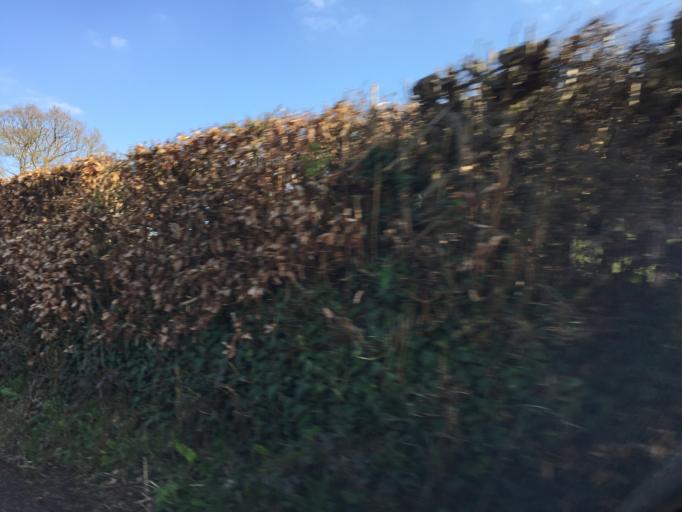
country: GB
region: Wales
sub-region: Torfaen County Borough
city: New Inn
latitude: 51.7052
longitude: -2.9771
